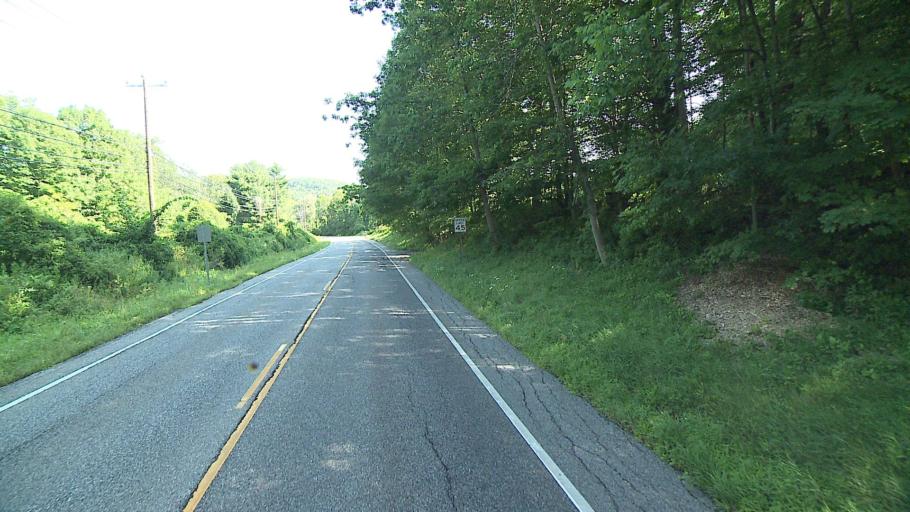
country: US
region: Connecticut
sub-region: Litchfield County
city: Kent
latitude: 41.8489
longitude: -73.4413
